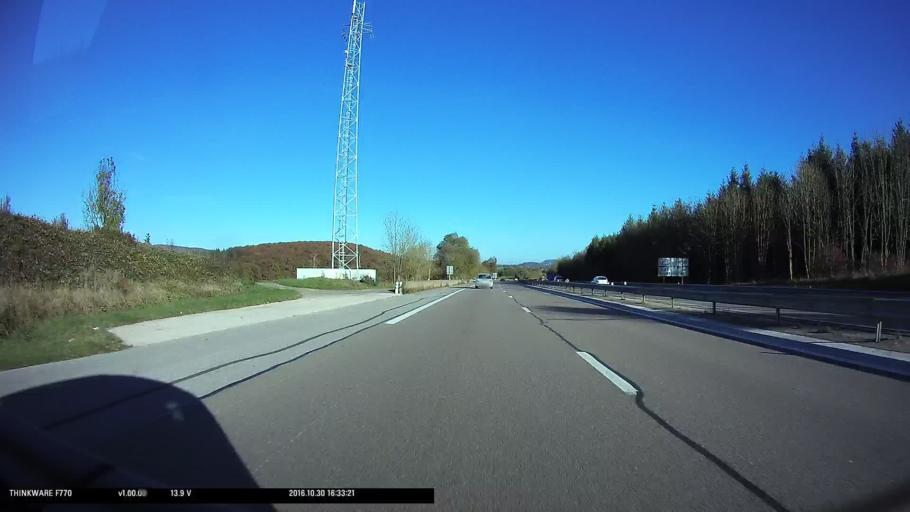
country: FR
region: Franche-Comte
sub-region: Departement du Doubs
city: Novillars
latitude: 47.3377
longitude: 6.1655
